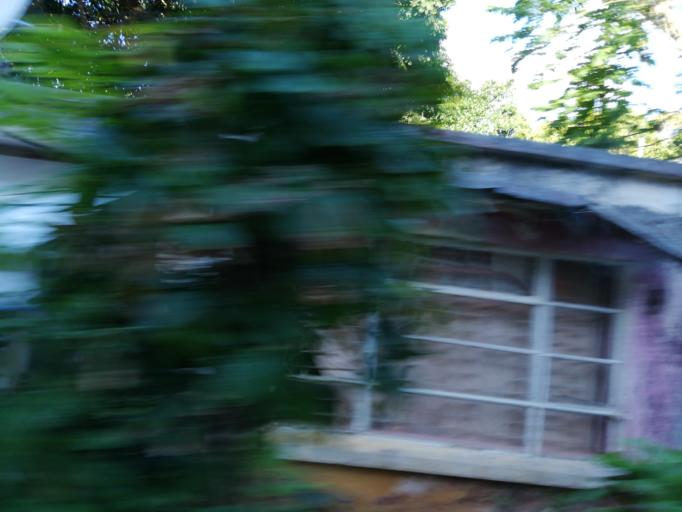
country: MU
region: Moka
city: Moka
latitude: -20.2235
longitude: 57.4699
